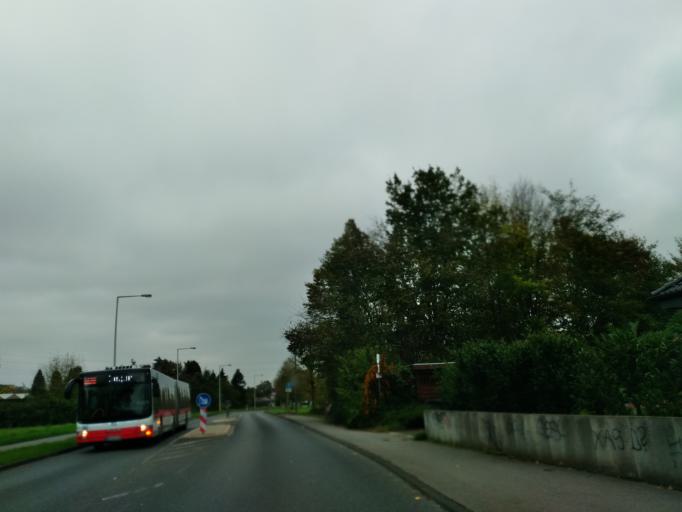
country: DE
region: North Rhine-Westphalia
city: Sankt Augustin
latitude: 50.7455
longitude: 7.1664
